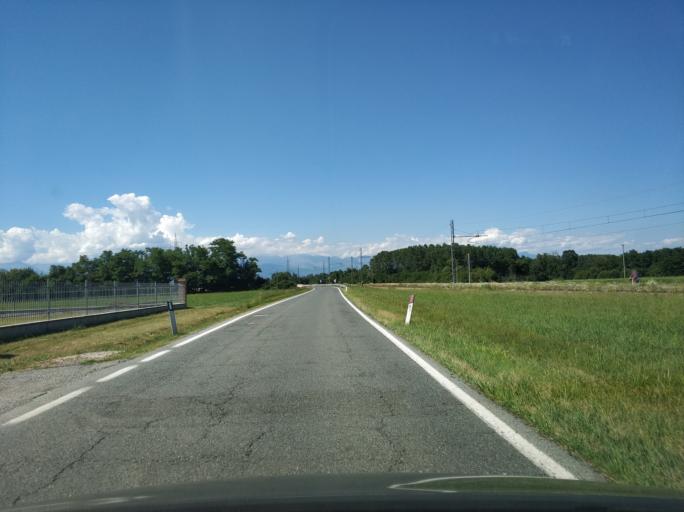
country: IT
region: Piedmont
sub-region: Provincia di Torino
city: San Benigno Canavese
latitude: 45.2407
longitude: 7.7731
